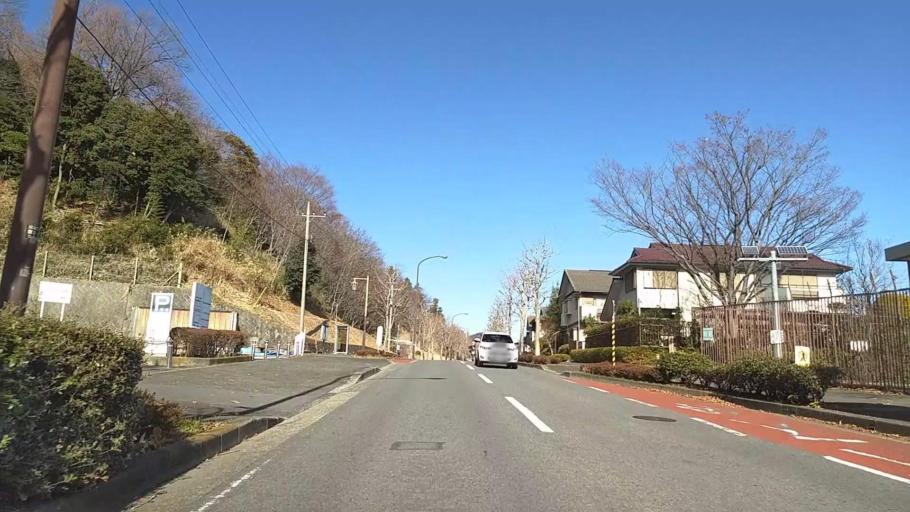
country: JP
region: Kanagawa
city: Atsugi
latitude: 35.4486
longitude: 139.3042
